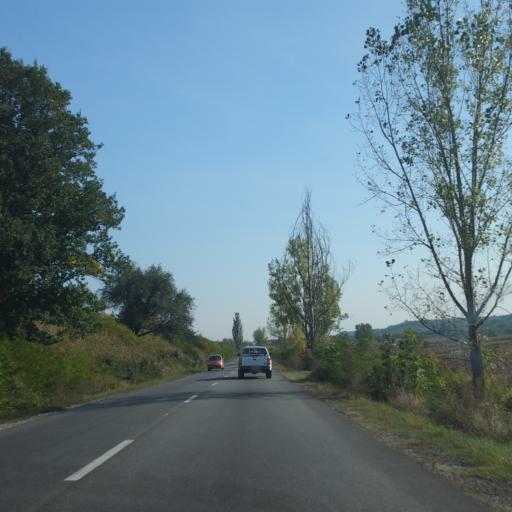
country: RO
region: Arges
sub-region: Comuna Merisani
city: Merisani
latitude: 44.9573
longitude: 24.7567
